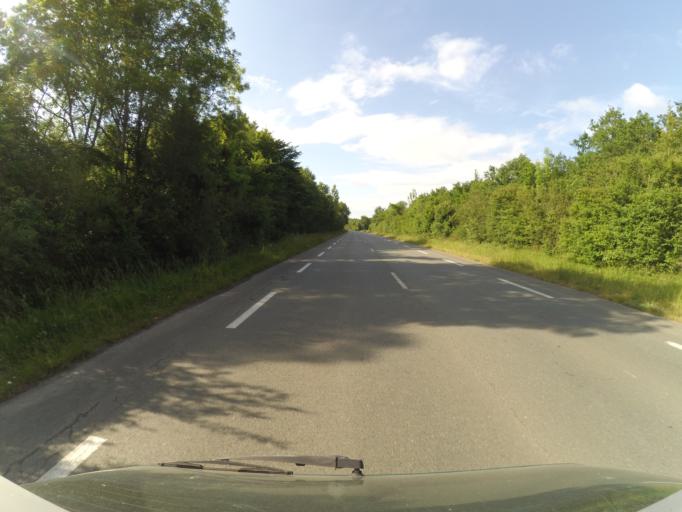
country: FR
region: Poitou-Charentes
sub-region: Departement de la Charente-Maritime
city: Saint-Agnant
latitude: 45.8192
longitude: -0.9314
